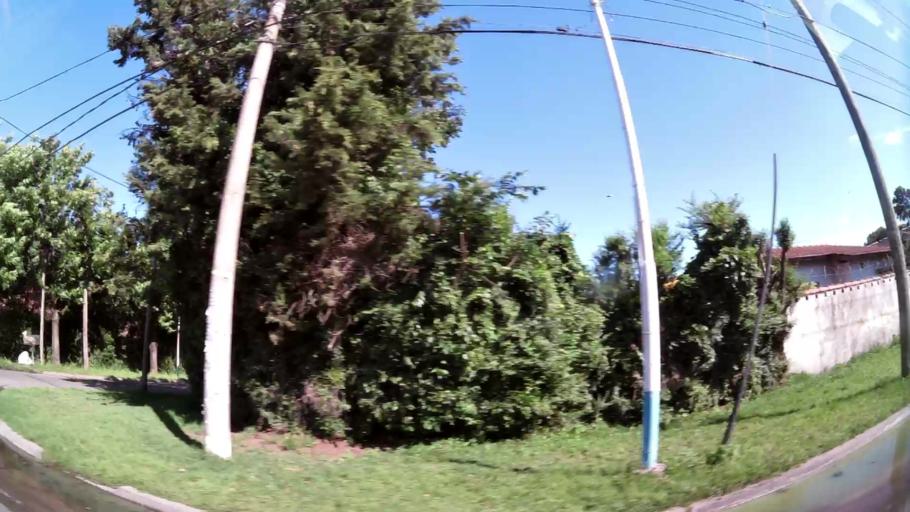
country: AR
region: Buenos Aires
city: Santa Catalina - Dique Lujan
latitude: -34.4921
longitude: -58.6912
